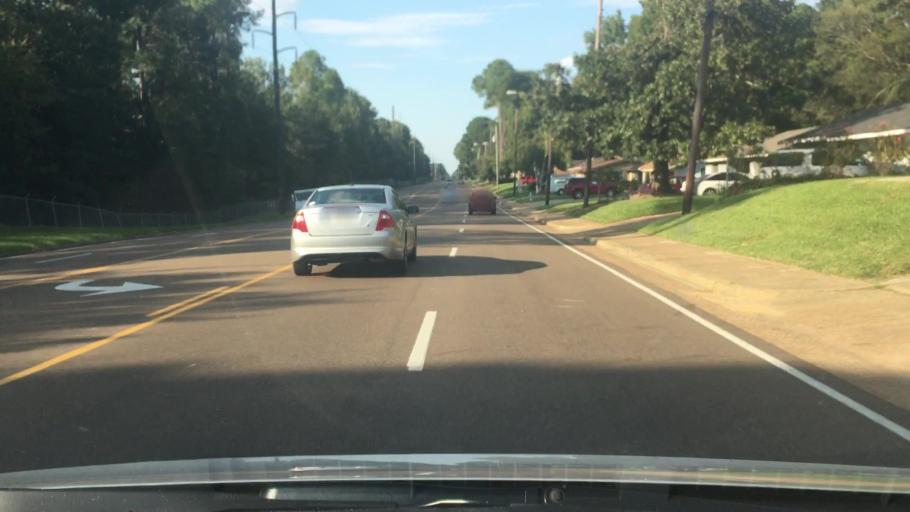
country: US
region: Mississippi
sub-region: Hinds County
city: Jackson
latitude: 32.3607
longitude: -90.1927
